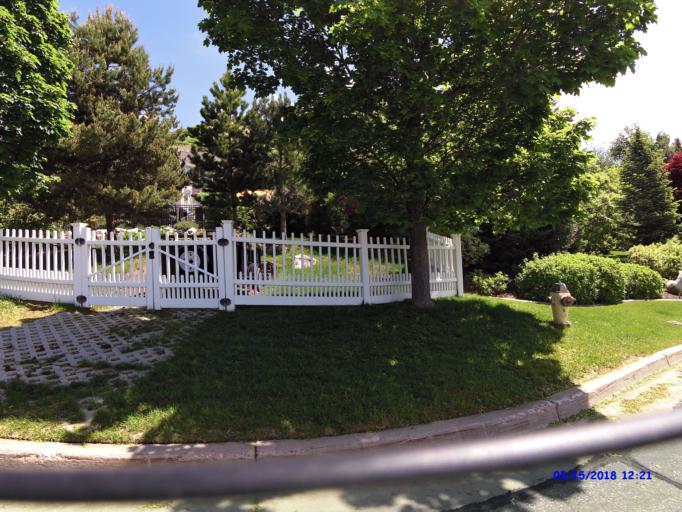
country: US
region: Utah
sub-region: Weber County
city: Uintah
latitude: 41.1667
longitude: -111.9238
